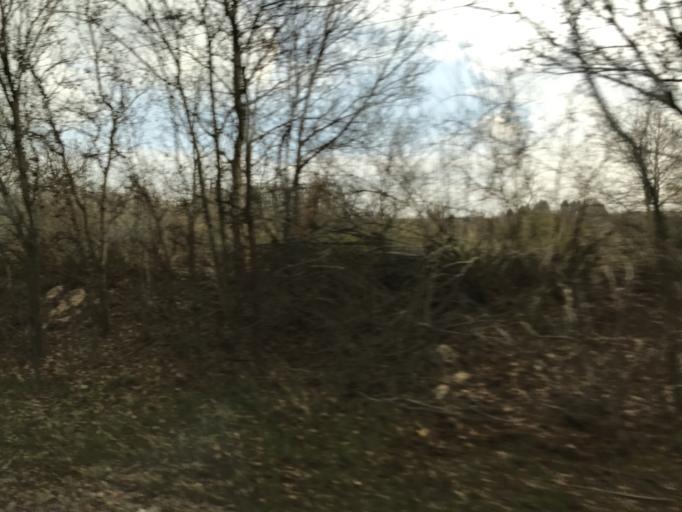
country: DE
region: Rheinland-Pfalz
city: Nieder-Ingelheim
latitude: 49.9923
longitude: 8.0778
